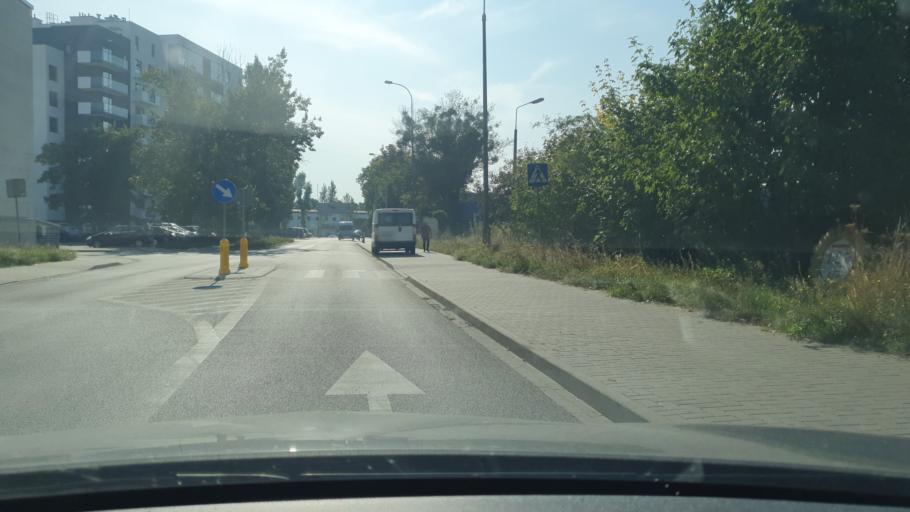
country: PL
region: Pomeranian Voivodeship
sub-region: Sopot
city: Sopot
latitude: 54.4023
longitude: 18.5871
